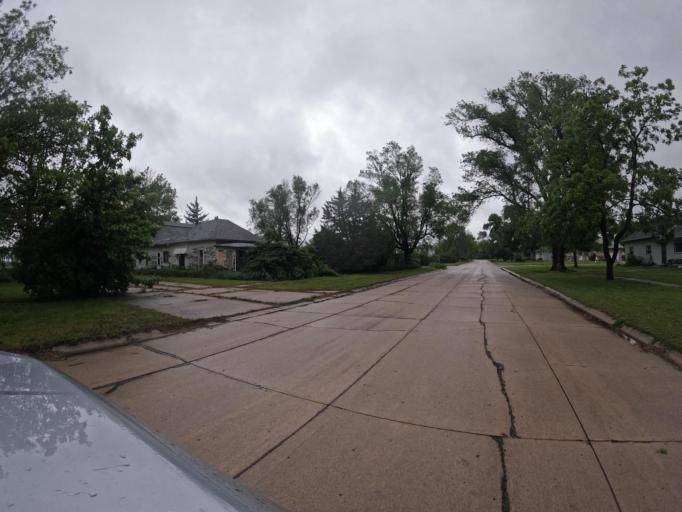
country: US
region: Nebraska
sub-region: Clay County
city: Harvard
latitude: 40.6239
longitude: -98.0985
